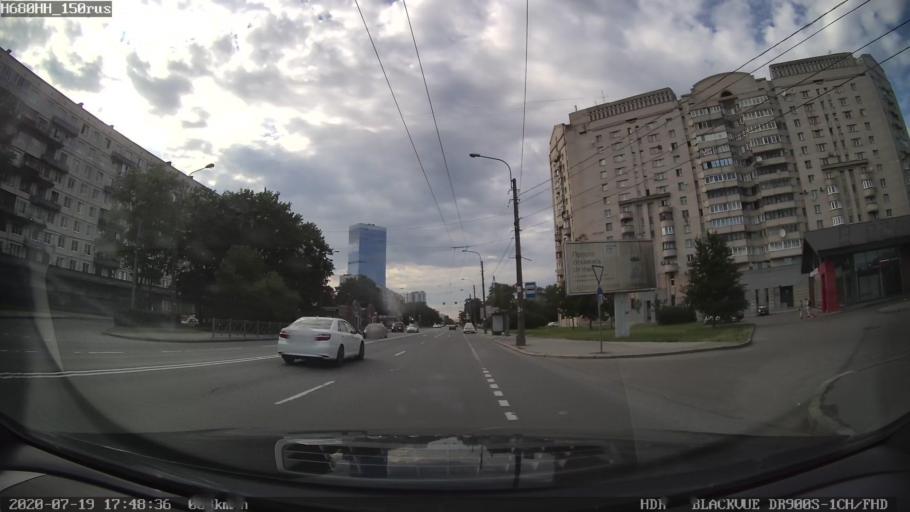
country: RU
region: St.-Petersburg
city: Kupchino
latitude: 59.8474
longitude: 30.3134
